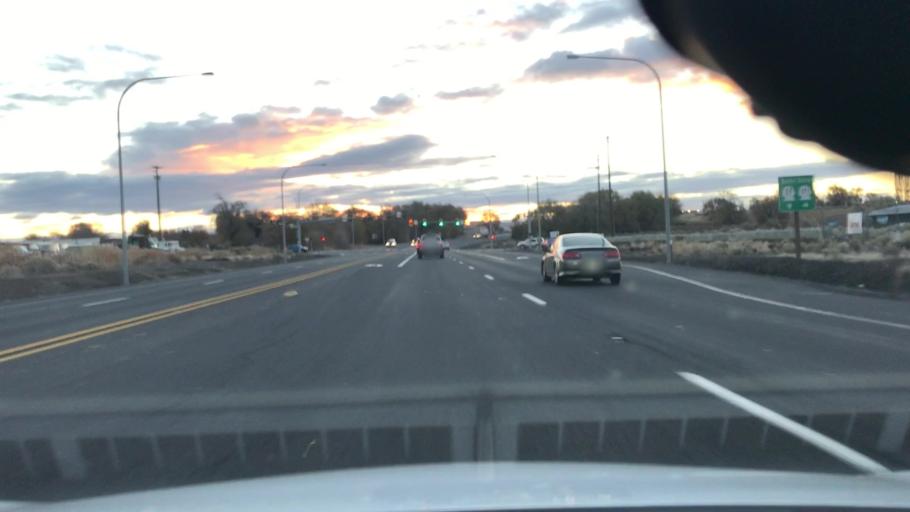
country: US
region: Washington
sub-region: Grant County
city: Moses Lake
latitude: 47.1403
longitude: -119.2643
